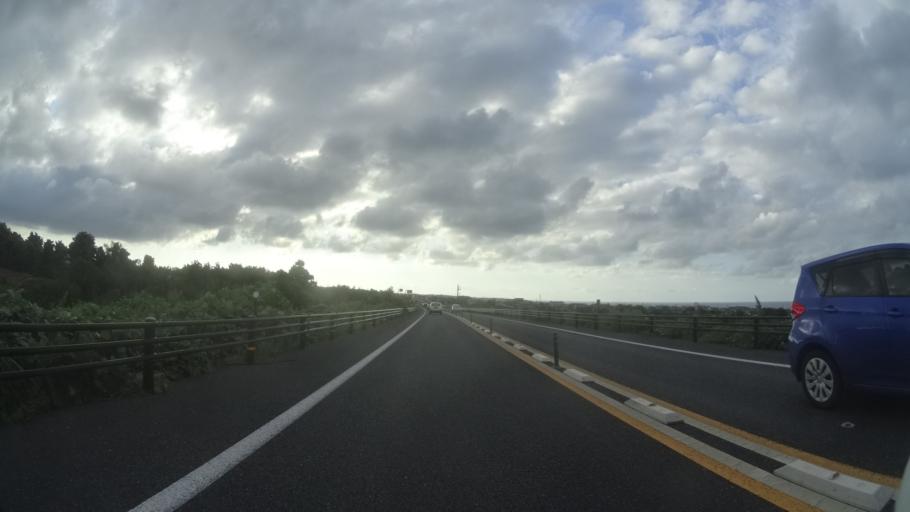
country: JP
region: Tottori
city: Kurayoshi
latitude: 35.5079
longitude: 133.6417
